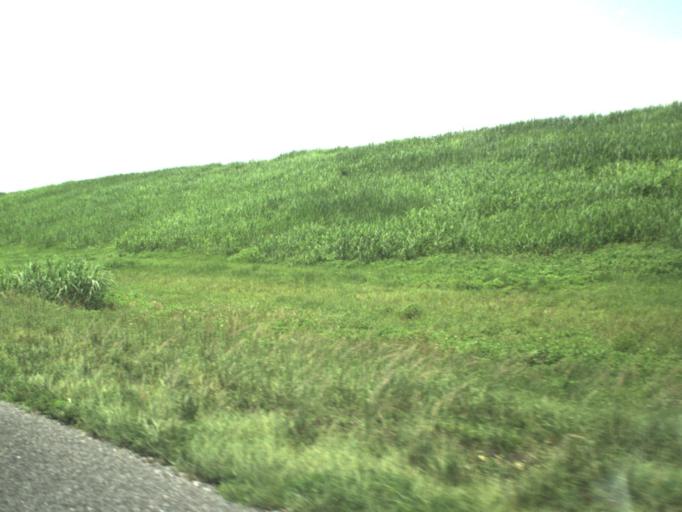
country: US
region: Florida
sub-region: Palm Beach County
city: South Bay
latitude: 26.6982
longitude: -80.7934
